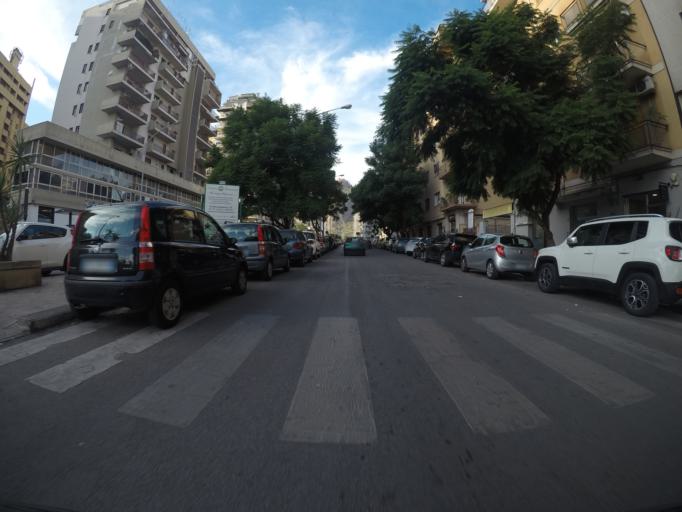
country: IT
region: Sicily
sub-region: Palermo
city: Palermo
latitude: 38.1393
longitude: 13.3582
